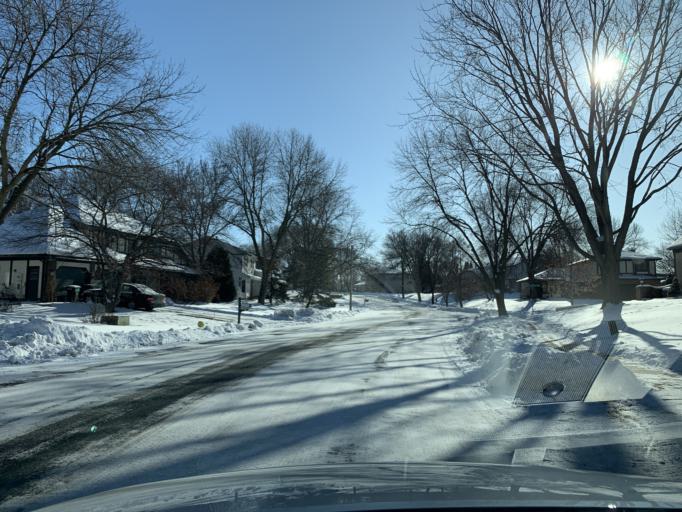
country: US
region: Minnesota
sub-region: Hennepin County
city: Edina
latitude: 44.8356
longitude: -93.3565
